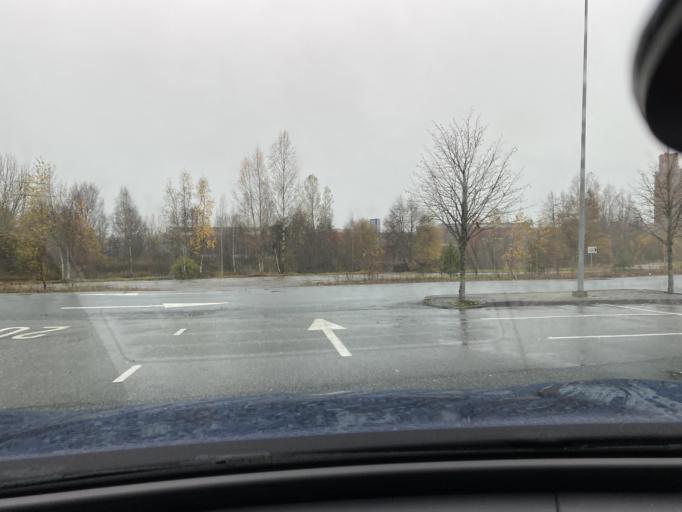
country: FI
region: Haeme
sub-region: Forssa
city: Forssa
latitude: 60.8114
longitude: 23.6383
